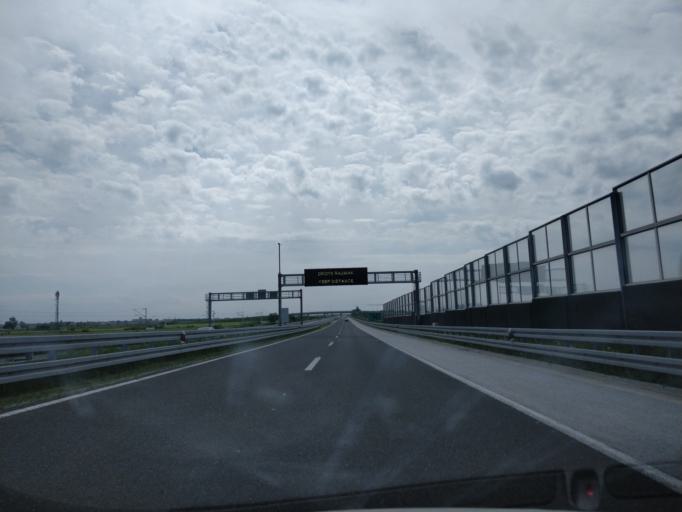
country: HR
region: Grad Zagreb
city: Odra
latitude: 45.7321
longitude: 16.0134
